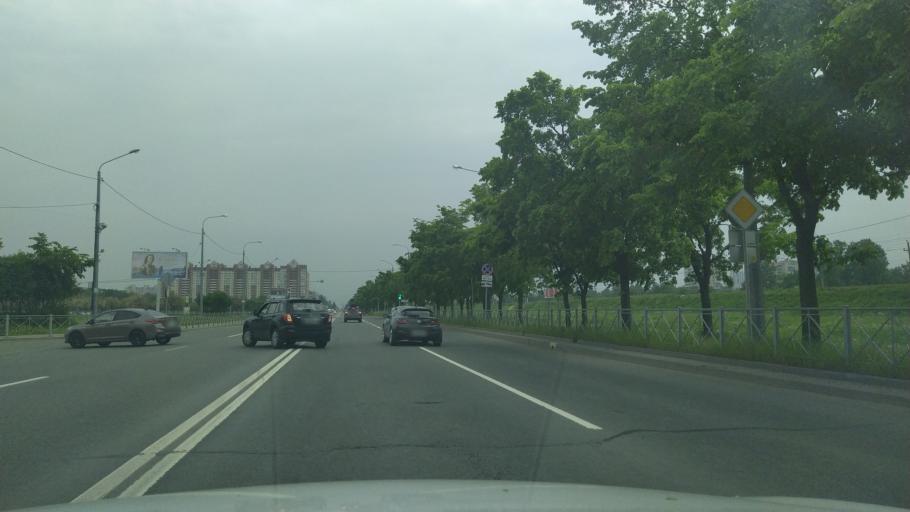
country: RU
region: St.-Petersburg
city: Kupchino
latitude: 59.8672
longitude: 30.3594
